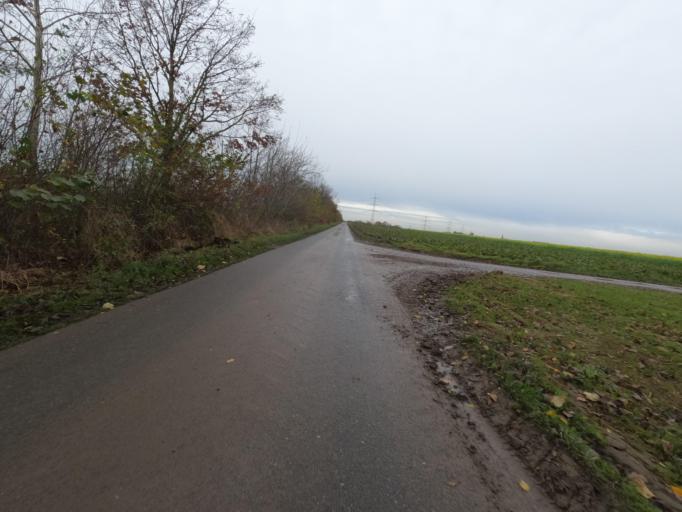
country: DE
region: North Rhine-Westphalia
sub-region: Regierungsbezirk Koln
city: Heinsberg
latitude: 51.0339
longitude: 6.1173
